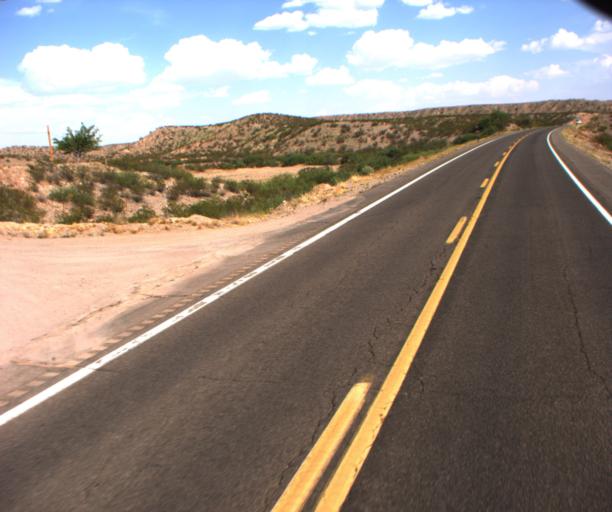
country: US
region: Arizona
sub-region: Greenlee County
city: Clifton
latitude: 32.8129
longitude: -109.1694
